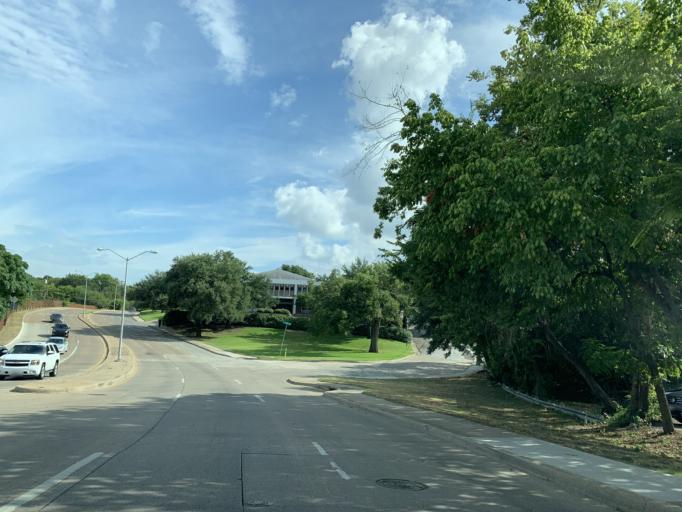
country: US
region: Texas
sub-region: Dallas County
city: Cockrell Hill
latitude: 32.7330
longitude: -96.8378
